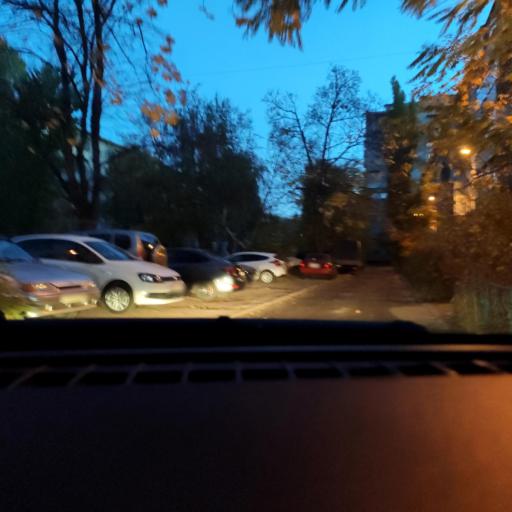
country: RU
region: Voronezj
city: Voronezh
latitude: 51.6814
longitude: 39.2651
